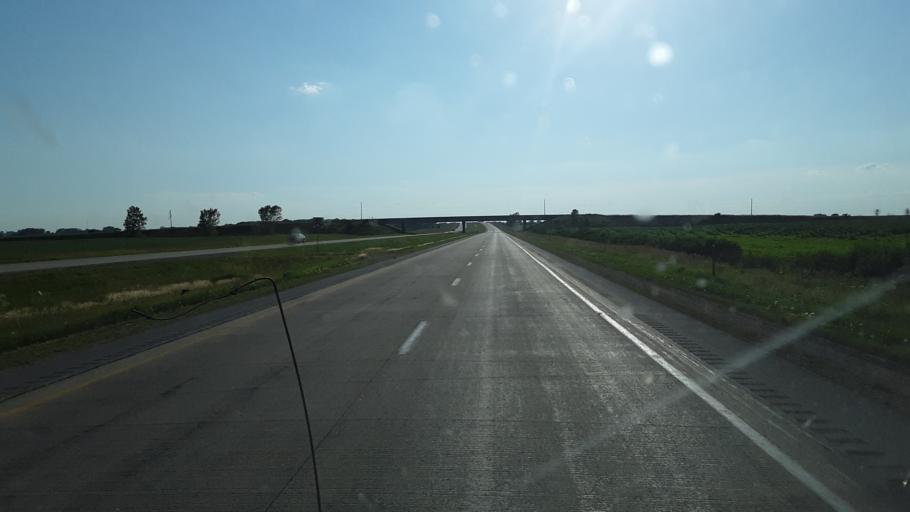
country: US
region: Iowa
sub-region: Hardin County
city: Iowa Falls
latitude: 42.4486
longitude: -93.3424
